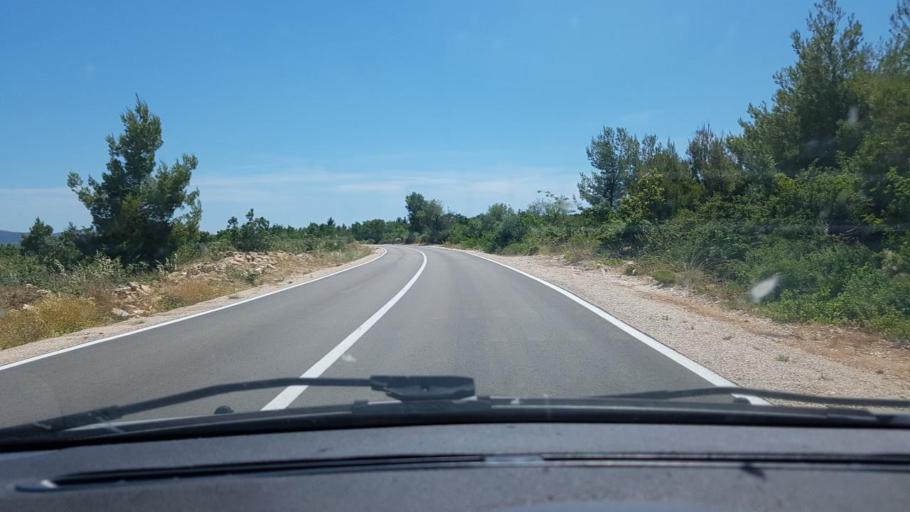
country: HR
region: Sibensko-Kniniska
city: Kistanje
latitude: 43.8752
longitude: 15.9126
